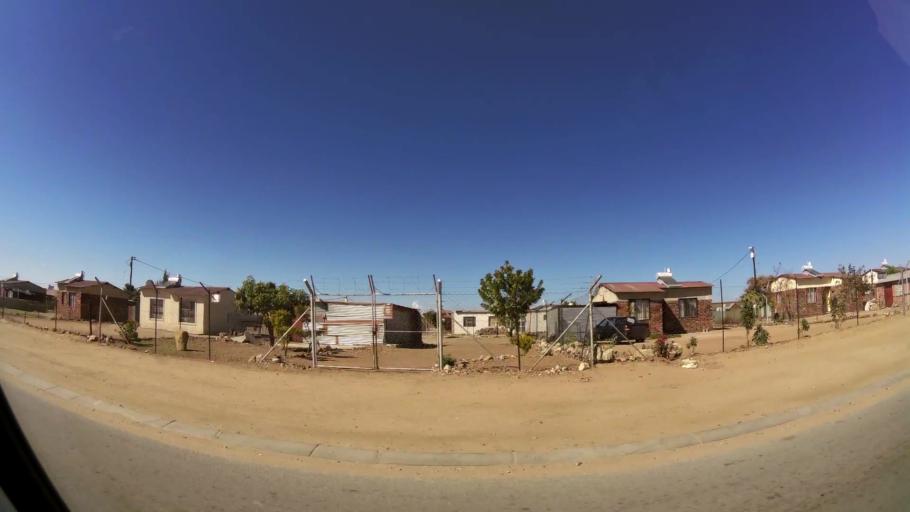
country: ZA
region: Limpopo
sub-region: Capricorn District Municipality
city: Polokwane
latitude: -23.8572
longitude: 29.4128
